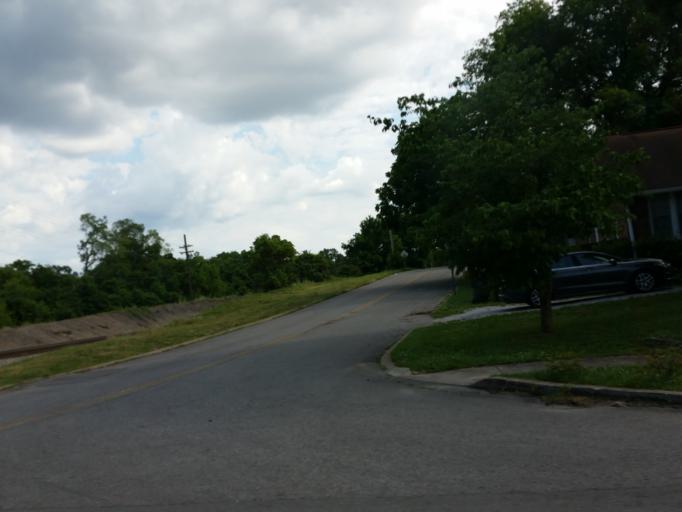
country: US
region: Tennessee
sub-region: Davidson County
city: Nashville
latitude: 36.2047
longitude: -86.7351
